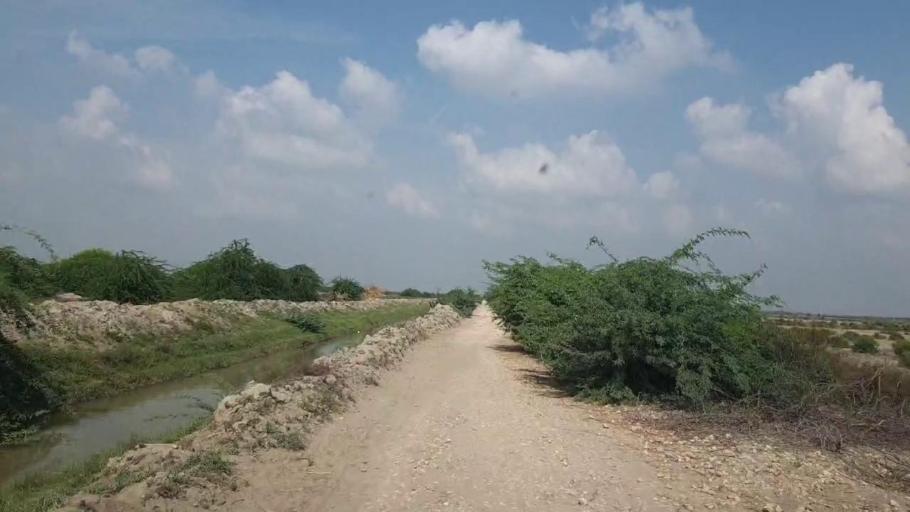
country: PK
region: Sindh
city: Badin
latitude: 24.4994
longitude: 68.6557
